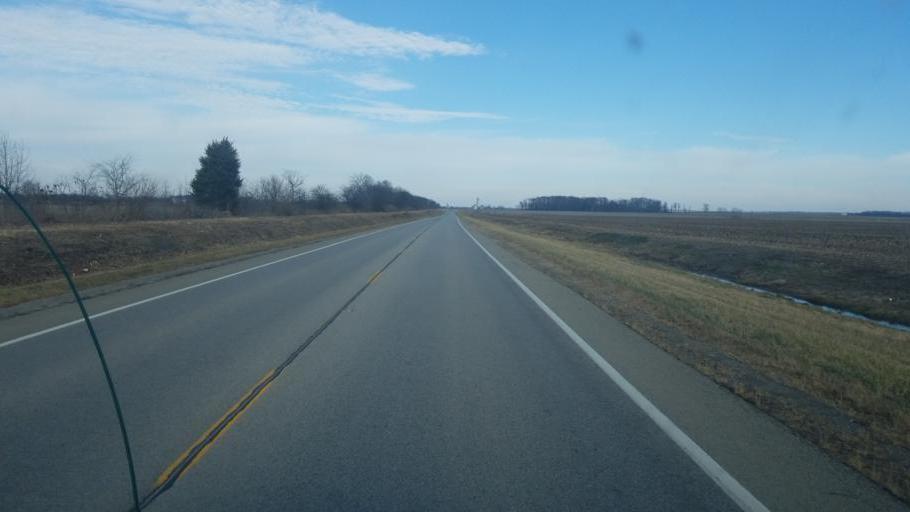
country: US
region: Illinois
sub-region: White County
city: Carmi
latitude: 38.1274
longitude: -88.1033
